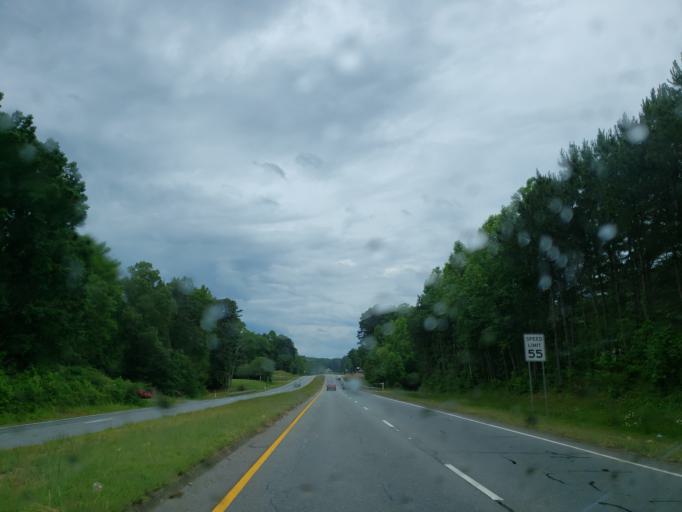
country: US
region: Georgia
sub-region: Haralson County
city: Buchanan
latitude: 33.7651
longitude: -85.1668
